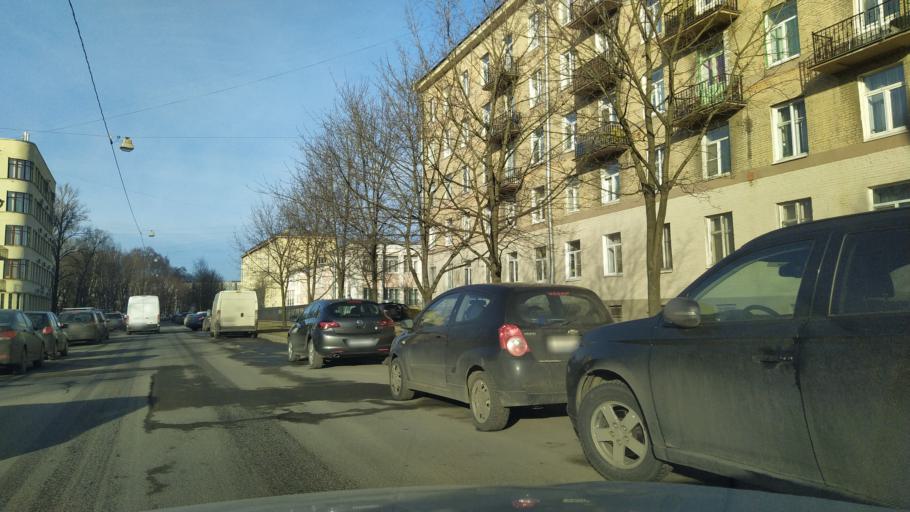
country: RU
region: St.-Petersburg
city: Kupchino
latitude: 59.8763
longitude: 30.3313
